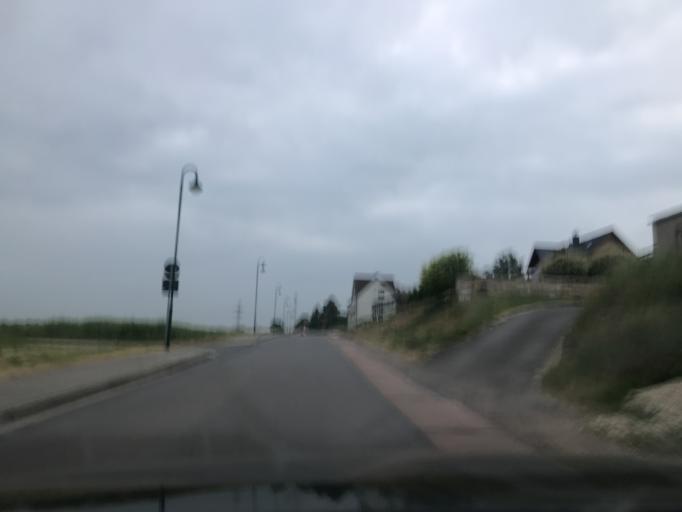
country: DE
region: Saxony-Anhalt
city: Angersdorf
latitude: 51.4566
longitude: 11.8988
